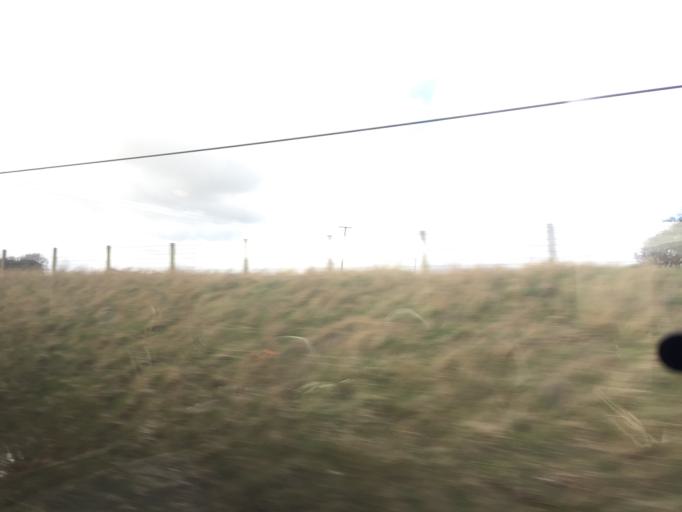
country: GB
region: Scotland
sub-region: South Lanarkshire
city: Forth
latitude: 55.6905
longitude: -3.7051
